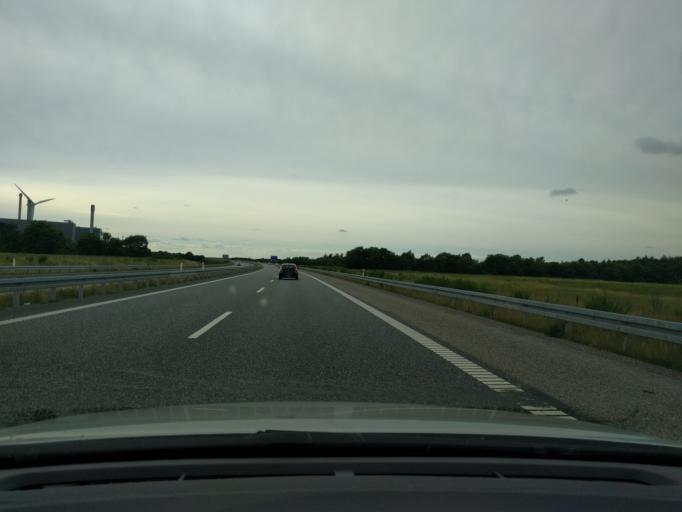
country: DK
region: Central Jutland
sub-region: Ikast-Brande Kommune
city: Brande
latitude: 55.9566
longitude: 9.1351
